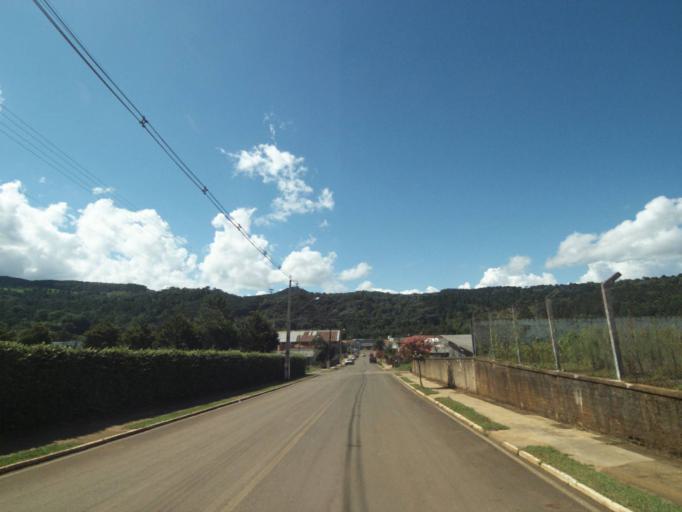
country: BR
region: Parana
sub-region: Uniao Da Vitoria
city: Uniao da Vitoria
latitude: -26.1529
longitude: -51.5475
